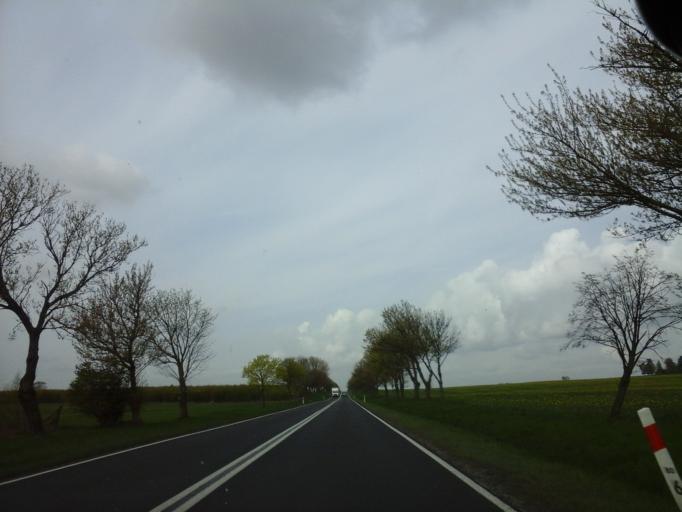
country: PL
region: West Pomeranian Voivodeship
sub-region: Powiat choszczenski
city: Recz
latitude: 53.2661
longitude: 15.5134
